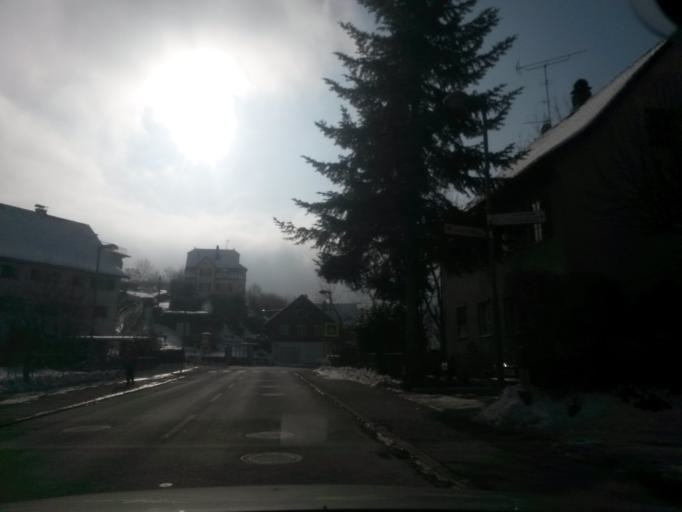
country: AT
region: Vorarlberg
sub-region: Politischer Bezirk Bregenz
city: Lochau
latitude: 47.5266
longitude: 9.7514
